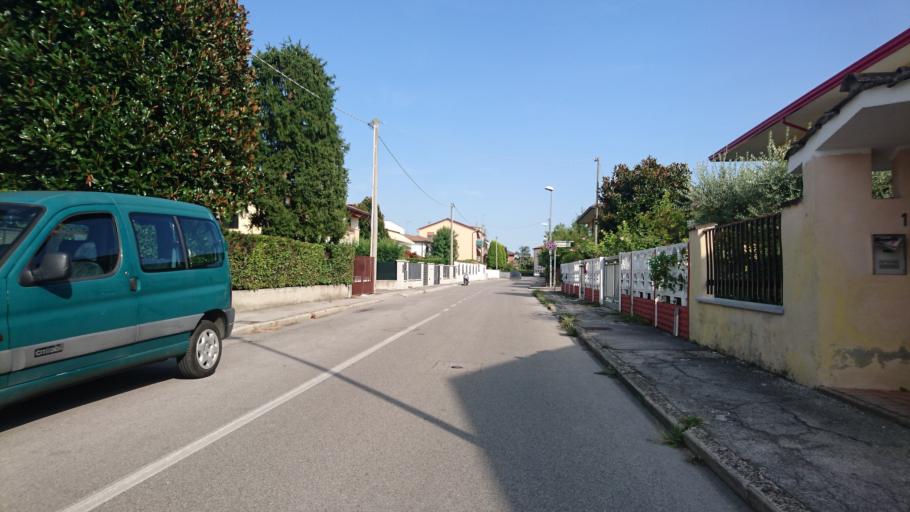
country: IT
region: Veneto
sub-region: Provincia di Padova
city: Tencarola
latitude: 45.3954
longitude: 11.8014
